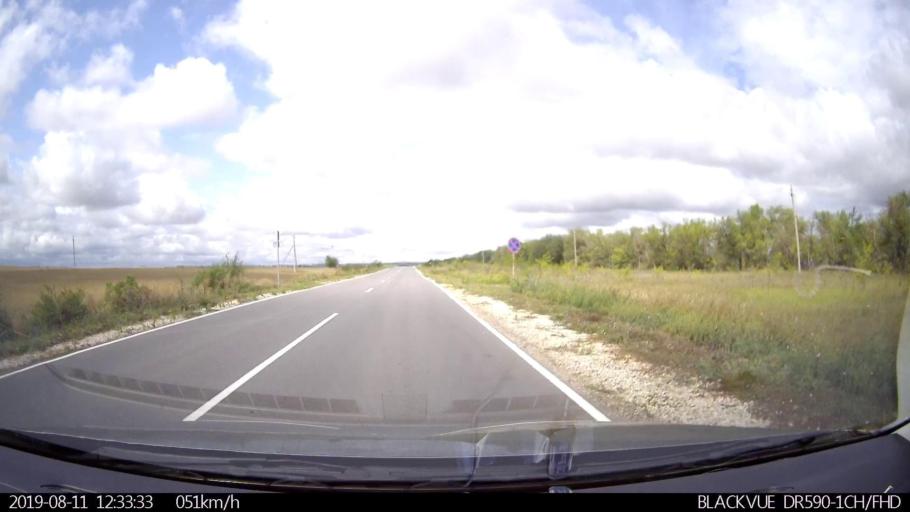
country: RU
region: Ulyanovsk
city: Ignatovka
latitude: 53.8103
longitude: 47.8544
